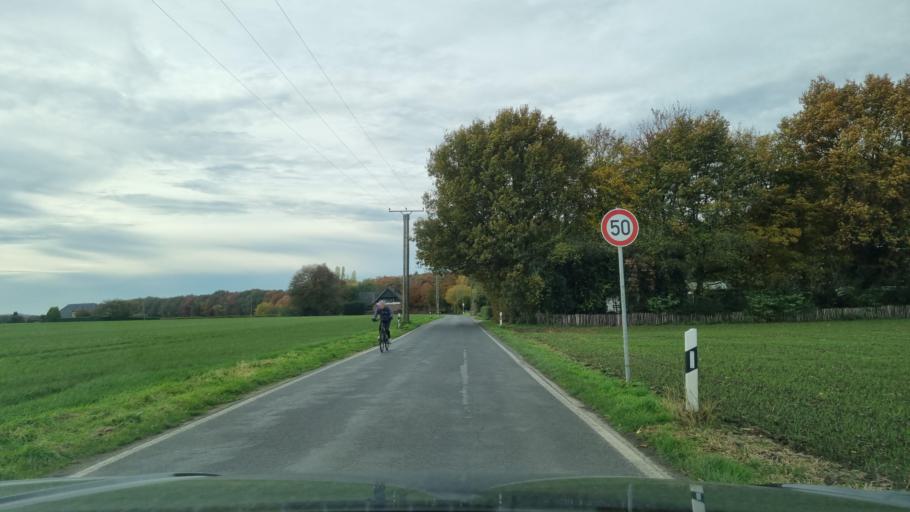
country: DE
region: North Rhine-Westphalia
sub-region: Regierungsbezirk Dusseldorf
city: Kranenburg
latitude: 51.7762
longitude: 5.9986
